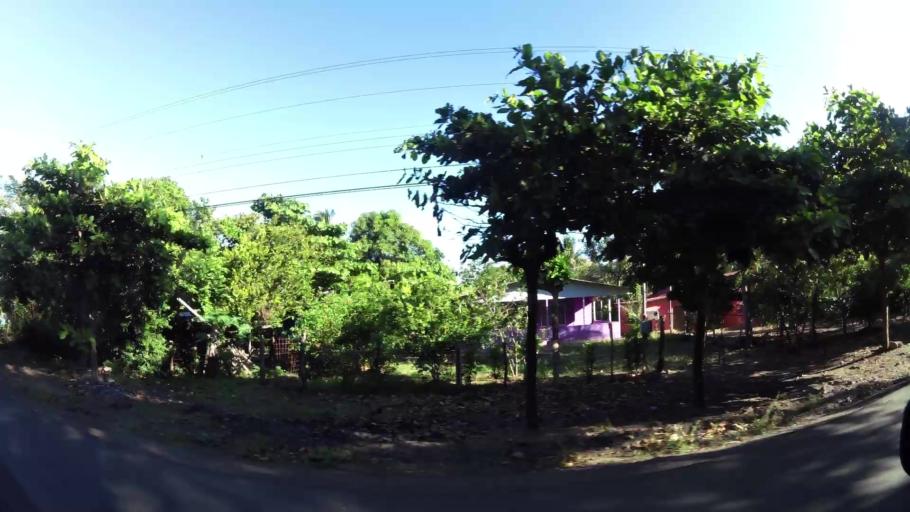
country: CR
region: Guanacaste
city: Sardinal
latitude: 10.4907
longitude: -85.6303
